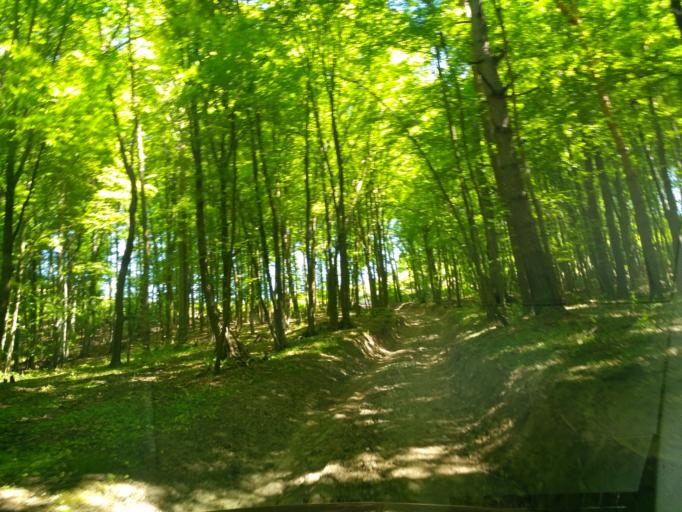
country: SK
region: Presovsky
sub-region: Okres Presov
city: Presov
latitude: 48.8774
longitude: 21.3881
